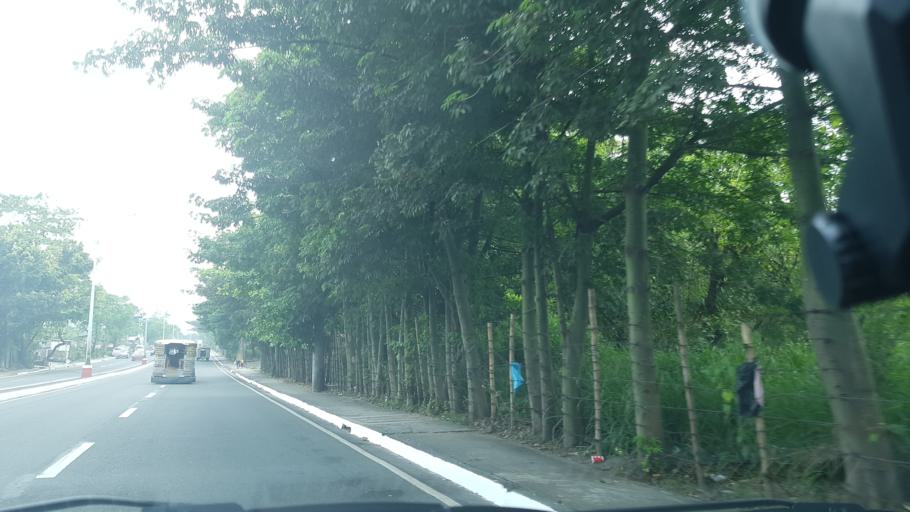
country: PH
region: Calabarzon
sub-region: Province of Rizal
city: San Mateo
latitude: 14.6839
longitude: 121.1051
